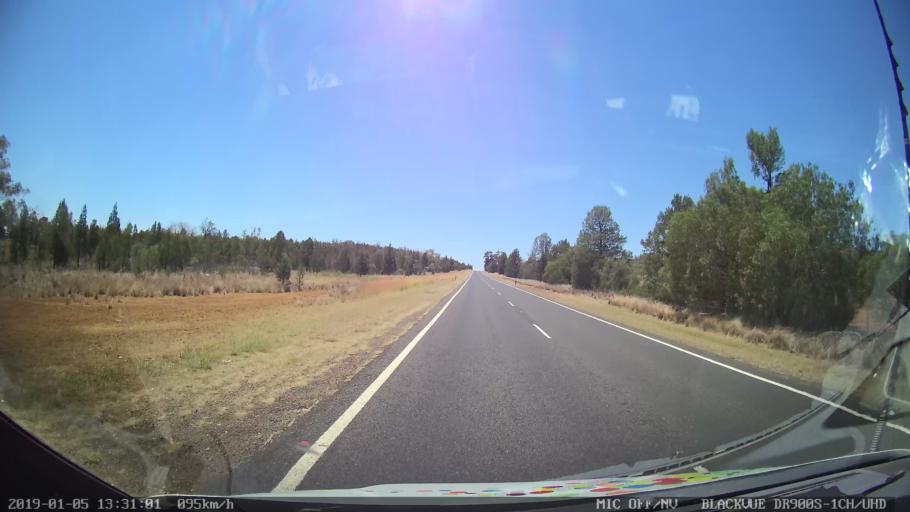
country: AU
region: New South Wales
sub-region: Gunnedah
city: Gunnedah
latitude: -31.0141
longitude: 150.0785
